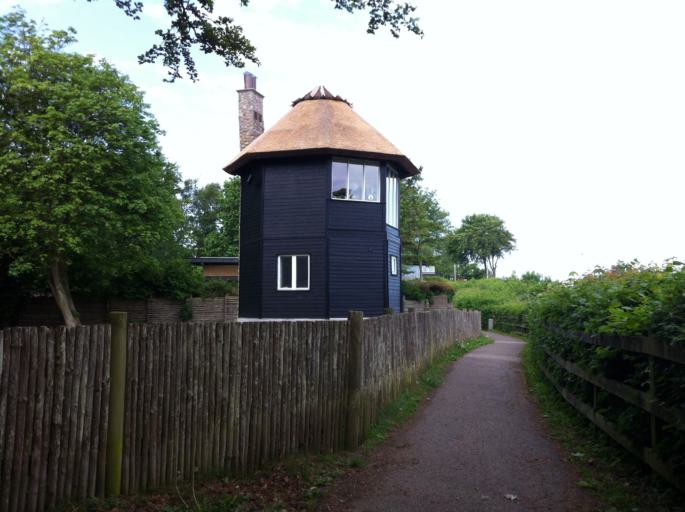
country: DK
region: Capital Region
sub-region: Gribskov Kommune
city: Gilleleje
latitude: 56.1277
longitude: 12.2913
